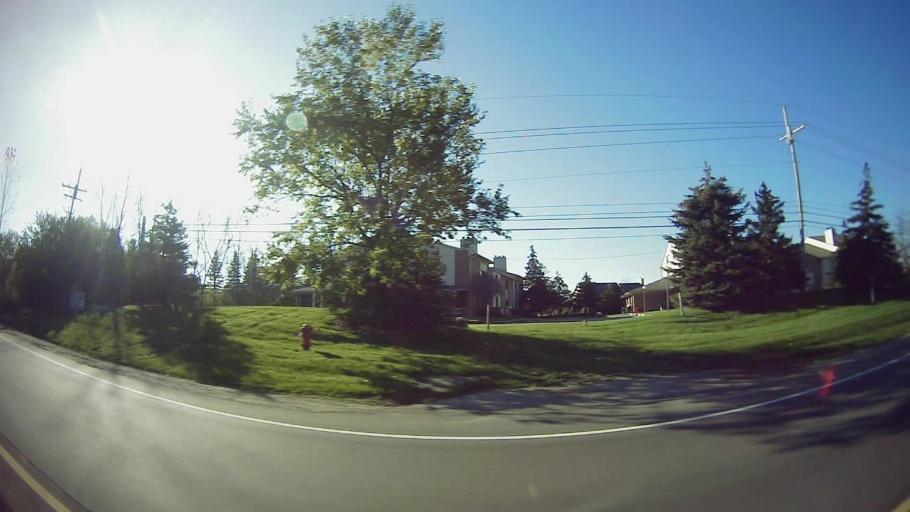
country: US
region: Michigan
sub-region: Oakland County
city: West Bloomfield Township
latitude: 42.5384
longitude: -83.3998
